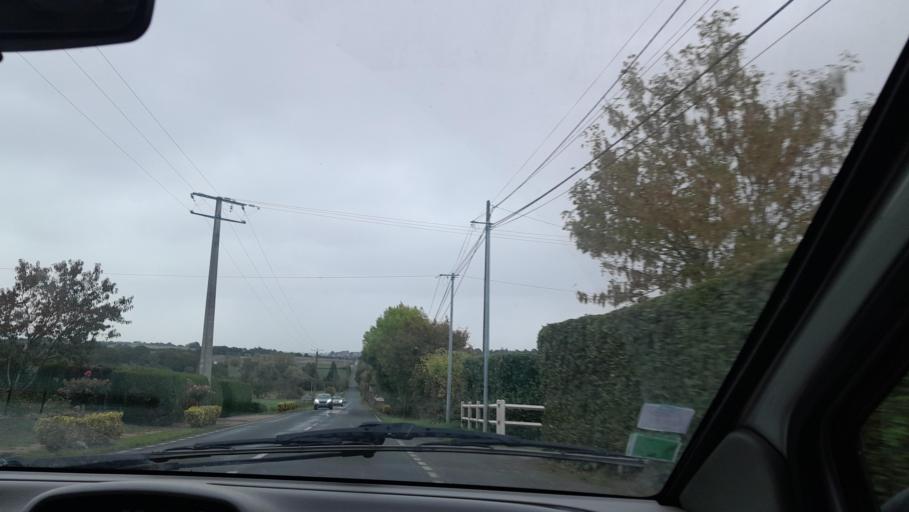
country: FR
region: Pays de la Loire
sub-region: Departement de Maine-et-Loire
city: Pouance
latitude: 47.7178
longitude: -1.1779
